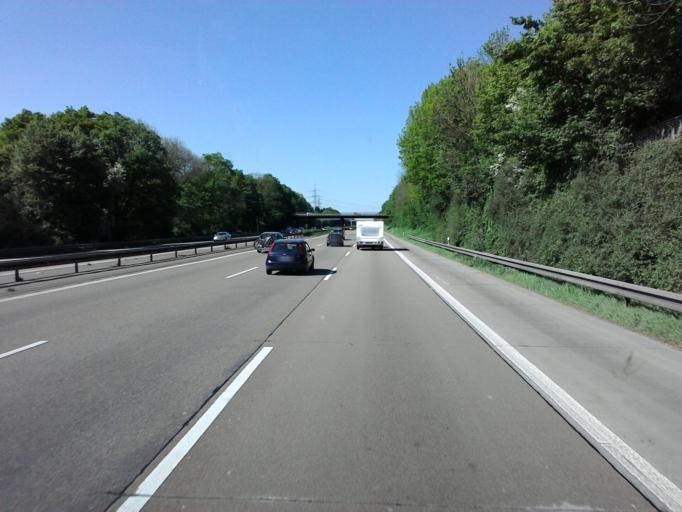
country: DE
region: North Rhine-Westphalia
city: Opladen
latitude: 51.0703
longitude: 6.9880
